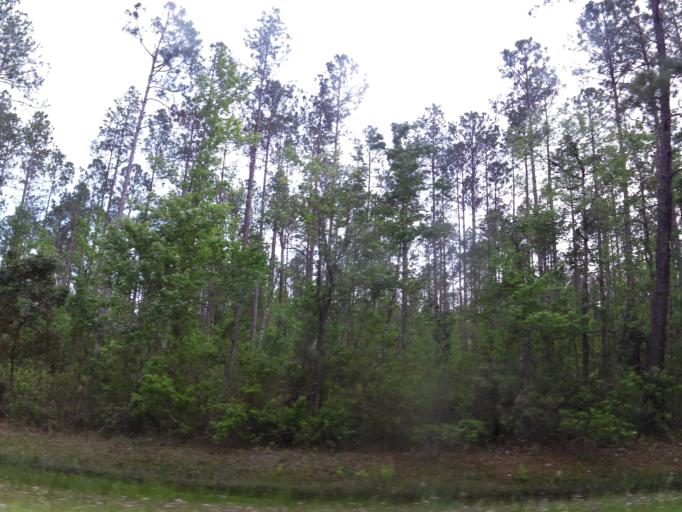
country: US
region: Florida
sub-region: Nassau County
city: Hilliard
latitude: 30.6966
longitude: -81.7981
